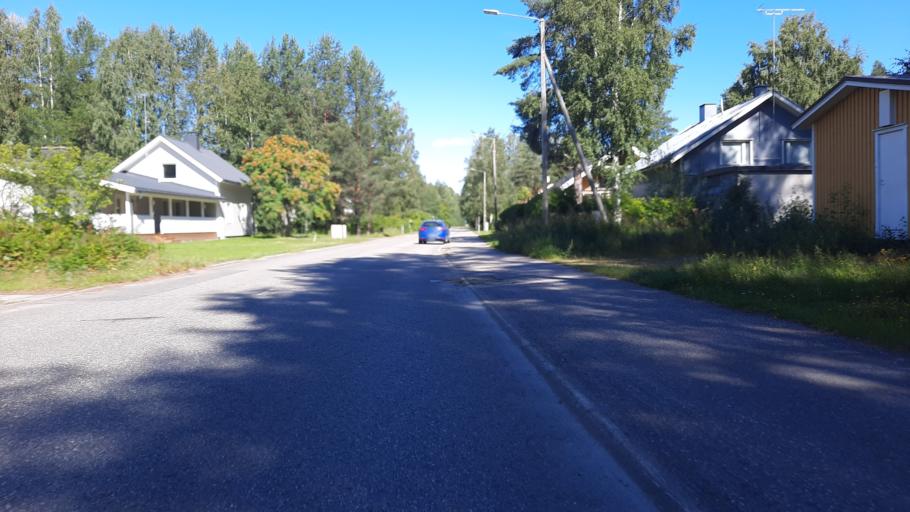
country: FI
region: North Karelia
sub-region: Joensuu
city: Joensuu
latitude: 62.6201
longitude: 29.7305
